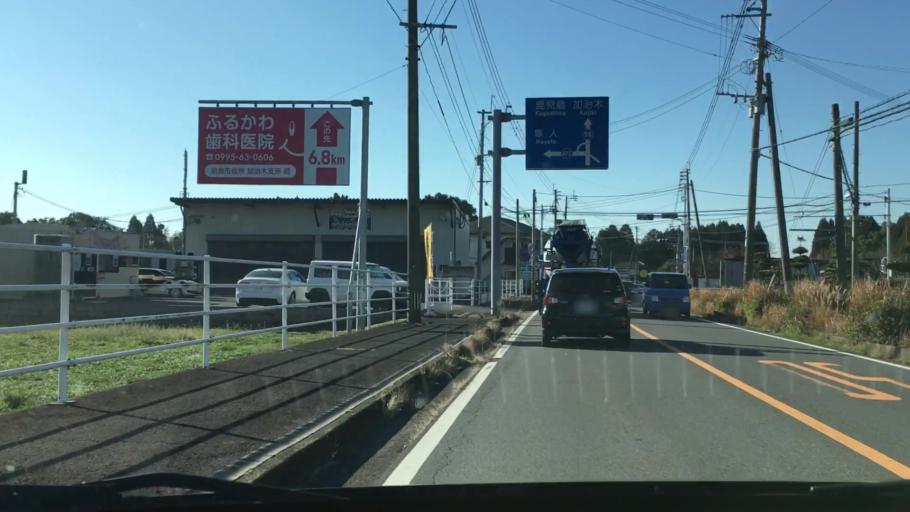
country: JP
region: Kagoshima
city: Kajiki
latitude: 31.7788
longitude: 130.7031
